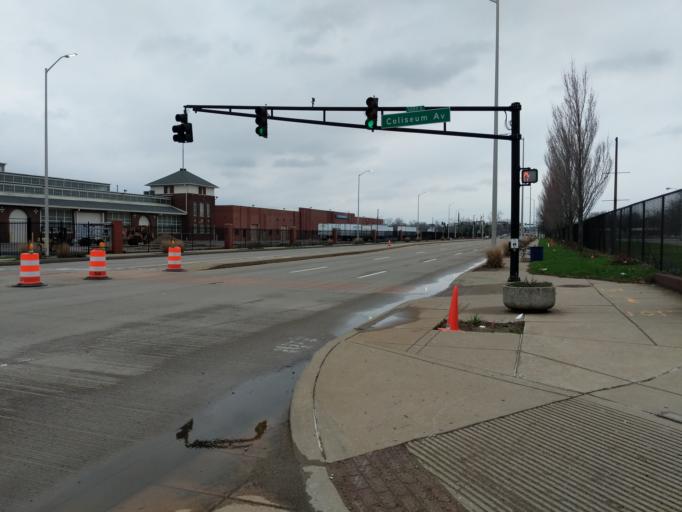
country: US
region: Indiana
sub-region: Marion County
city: Broad Ripple
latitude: 39.8253
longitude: -86.1370
